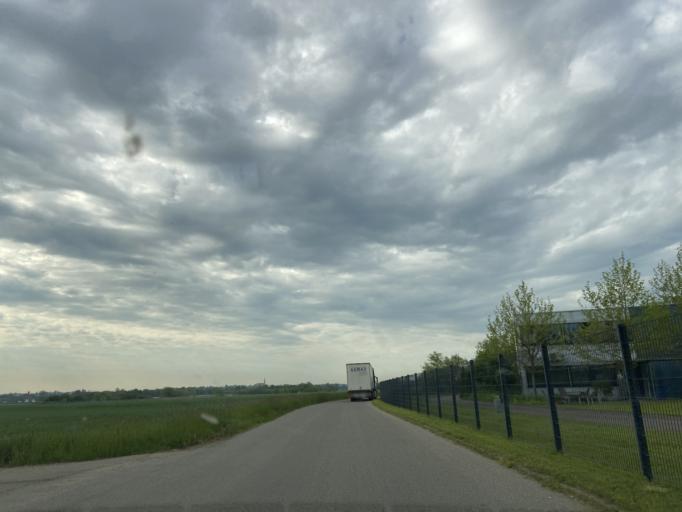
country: DE
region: Baden-Wuerttemberg
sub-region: Tuebingen Region
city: Mengen
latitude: 48.0539
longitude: 9.3571
